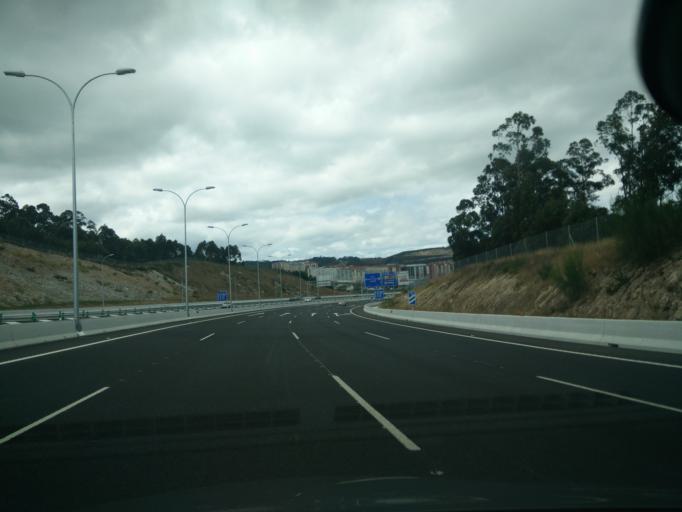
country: ES
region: Galicia
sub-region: Provincia da Coruna
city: Culleredo
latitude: 43.3245
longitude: -8.4161
